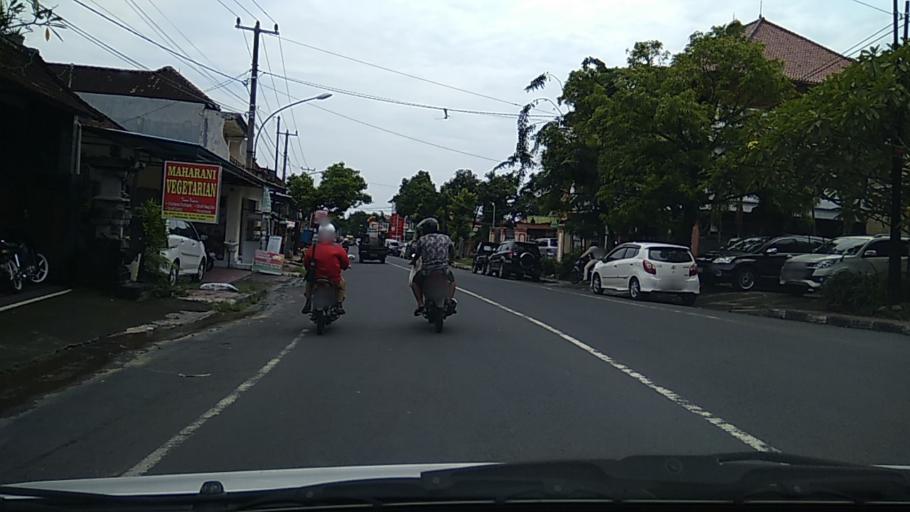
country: ID
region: Bali
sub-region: Kabupaten Gianyar
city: Ubud
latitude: -8.5347
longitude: 115.3055
